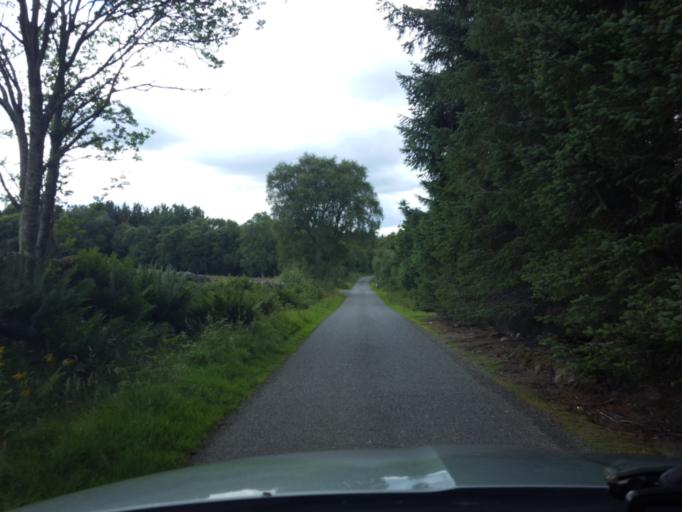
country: GB
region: Scotland
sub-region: Highland
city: Grantown on Spey
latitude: 57.3345
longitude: -3.5155
